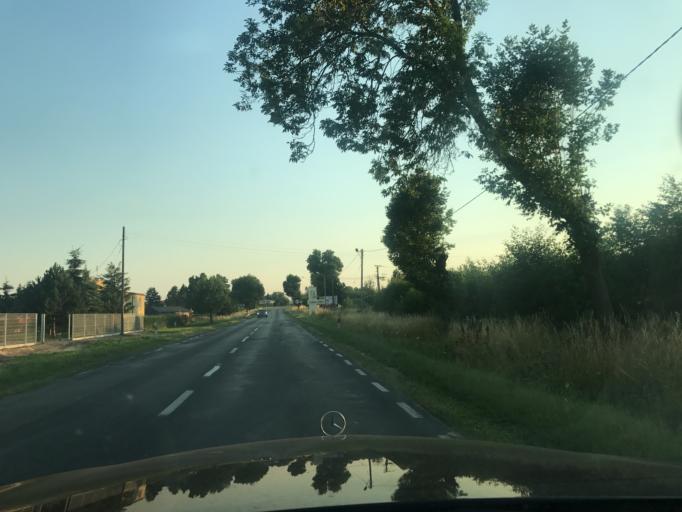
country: PL
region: Lublin Voivodeship
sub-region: Powiat lubartowski
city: Lubartow
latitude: 51.4762
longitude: 22.6127
